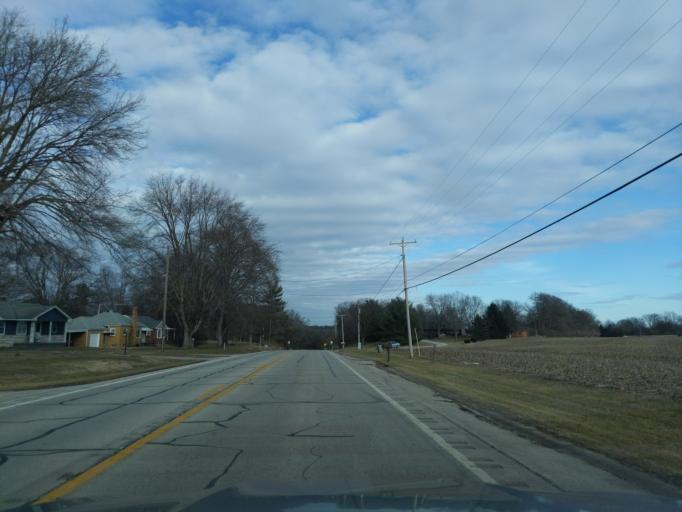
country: US
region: Indiana
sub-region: Tippecanoe County
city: Shadeland
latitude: 40.3754
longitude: -86.9453
